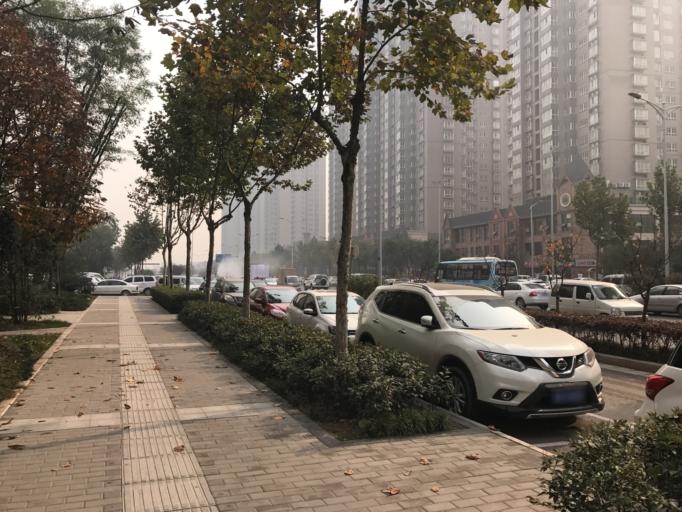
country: CN
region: Shaanxi
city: Xujia
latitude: 34.3544
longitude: 108.9462
